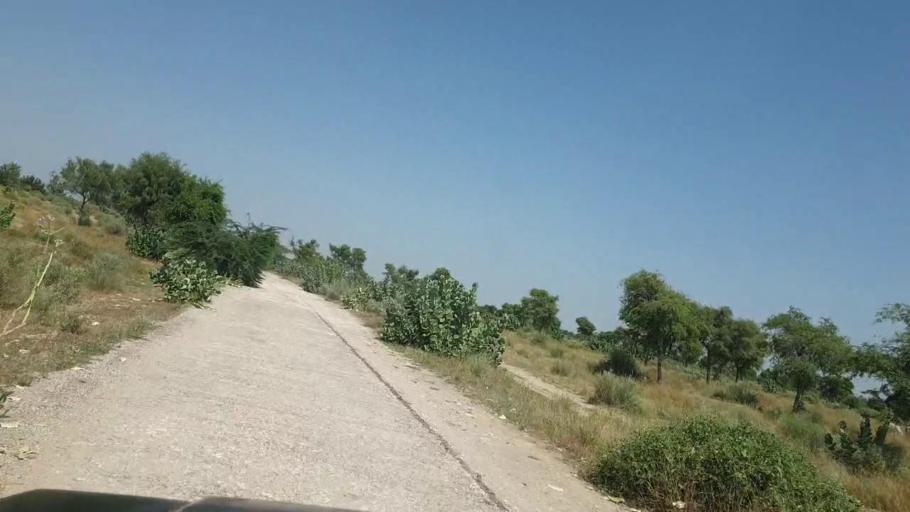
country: PK
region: Sindh
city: Chor
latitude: 25.3899
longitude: 70.3131
